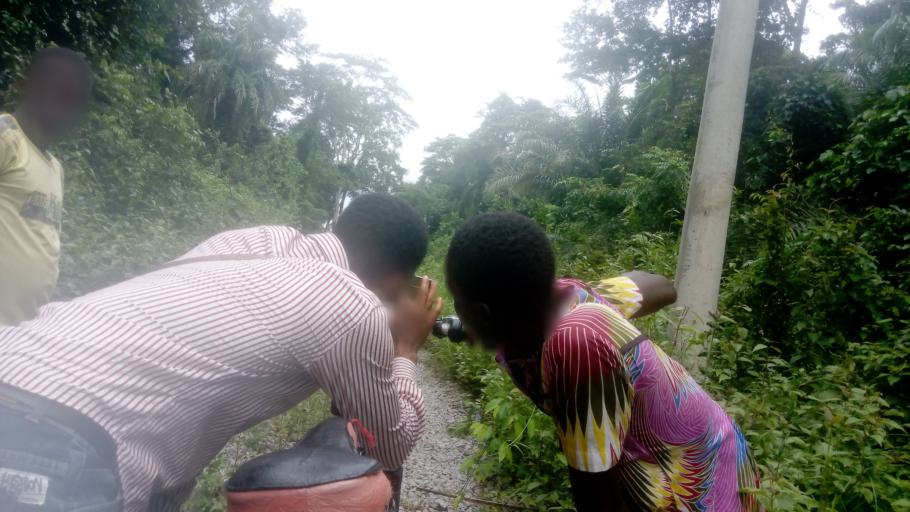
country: SL
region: Northern Province
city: Makali
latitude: 8.6287
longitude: -11.6545
